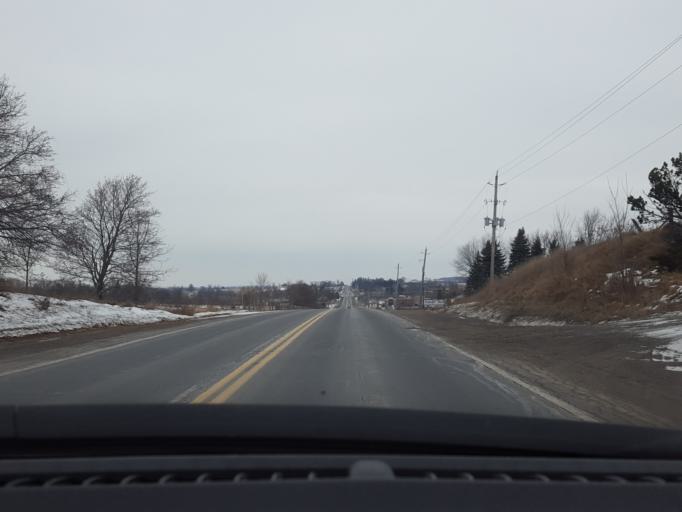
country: CA
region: Ontario
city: Newmarket
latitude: 44.1316
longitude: -79.4228
